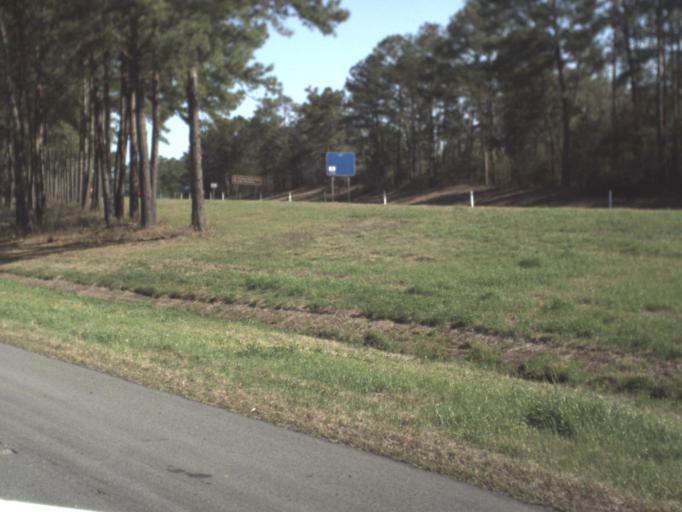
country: US
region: Florida
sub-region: Gadsden County
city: Chattahoochee
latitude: 30.6177
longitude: -84.8251
